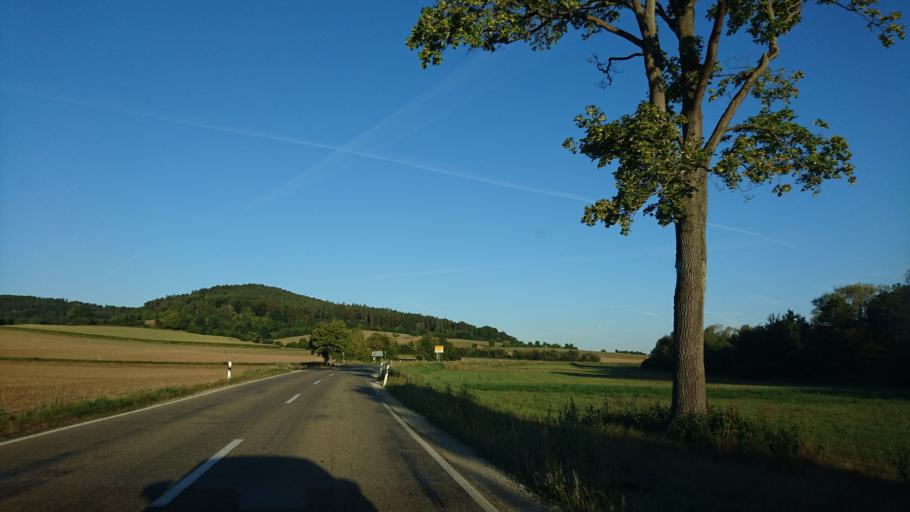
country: DE
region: Bavaria
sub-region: Regierungsbezirk Mittelfranken
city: Thalmassing
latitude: 49.0825
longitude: 11.2460
